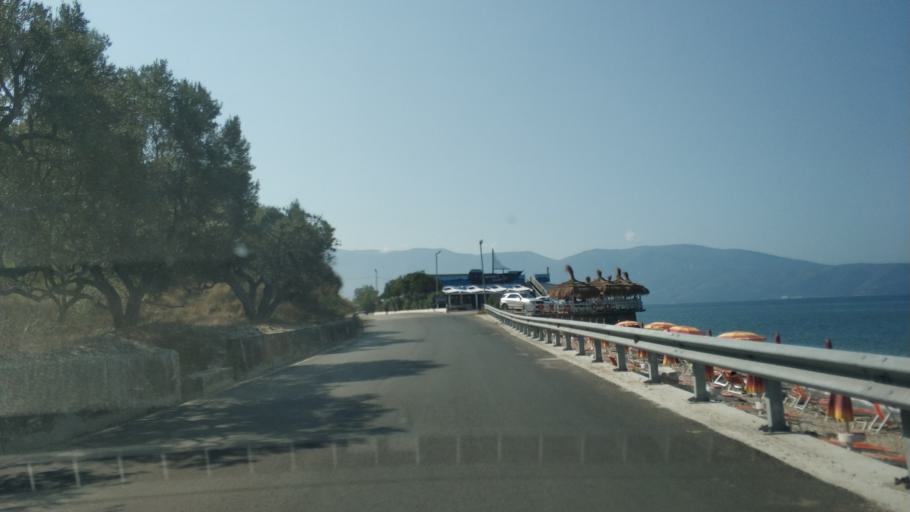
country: AL
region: Vlore
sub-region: Rrethi i Vlores
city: Orikum
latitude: 40.3676
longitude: 19.4818
